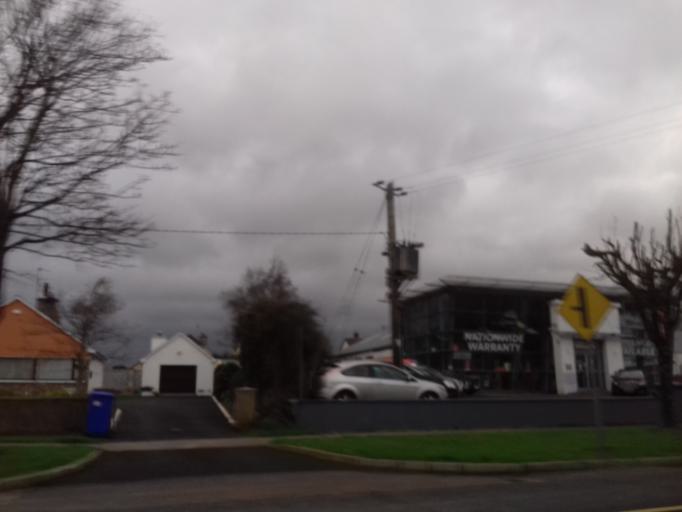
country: IE
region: Munster
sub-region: County Limerick
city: Newcastle West
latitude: 52.4522
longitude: -9.0449
